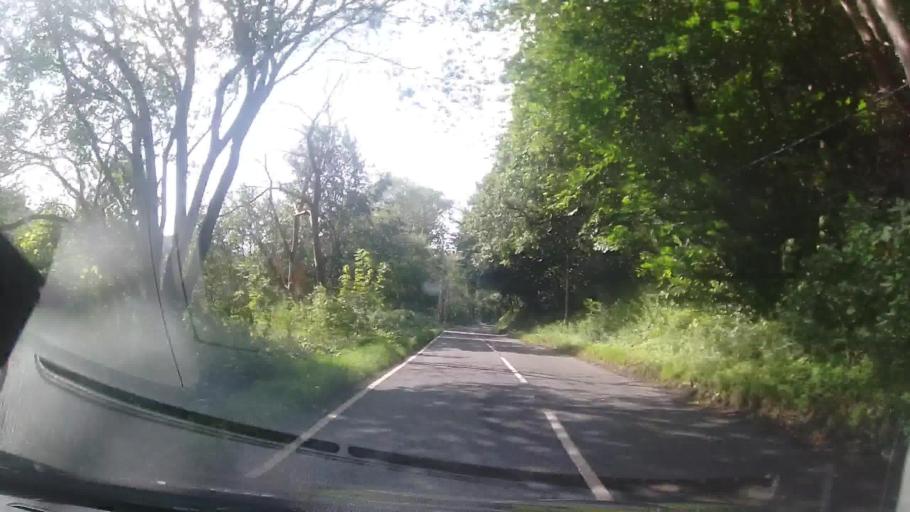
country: GB
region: Wales
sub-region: Sir Powys
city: Knighton
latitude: 52.3539
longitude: -3.0341
